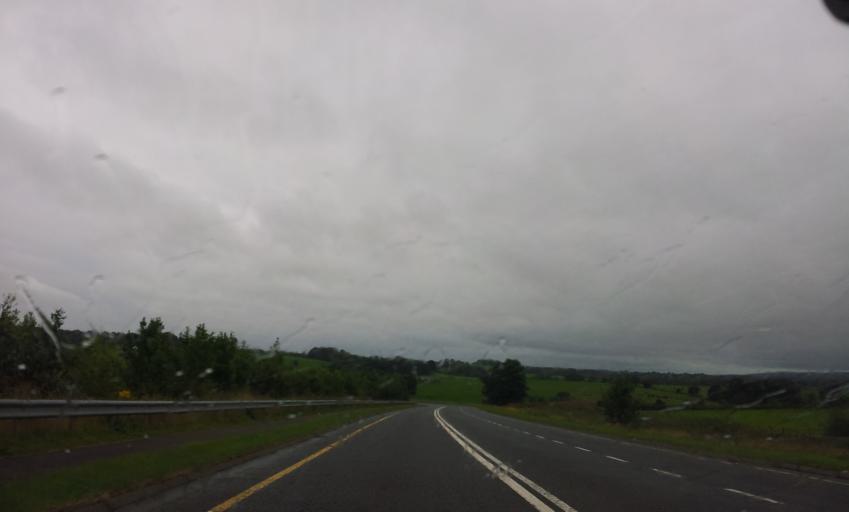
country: IE
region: Munster
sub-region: County Cork
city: Mitchelstown
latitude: 52.2728
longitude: -8.2856
